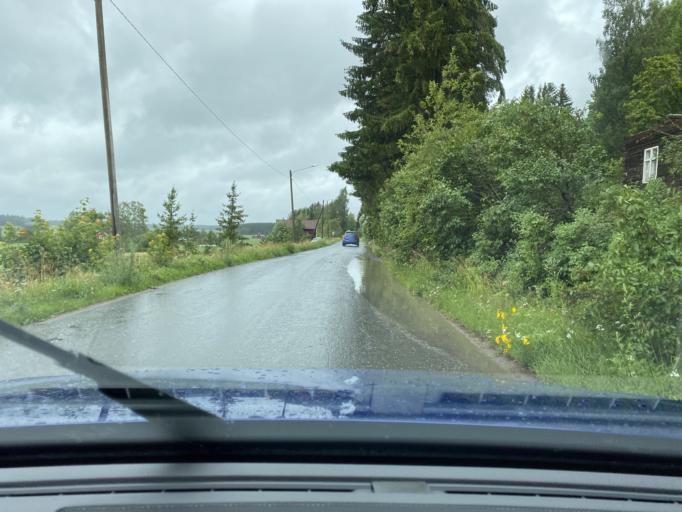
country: FI
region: Pirkanmaa
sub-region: Lounais-Pirkanmaa
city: Punkalaidun
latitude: 61.1485
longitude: 23.1901
